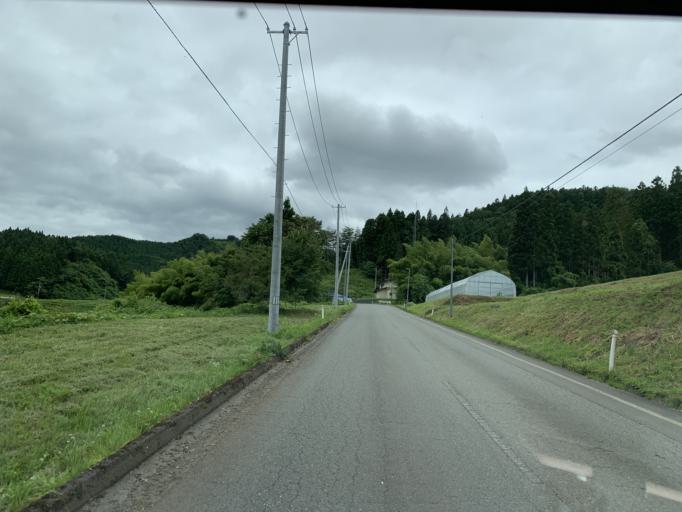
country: JP
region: Iwate
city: Ichinoseki
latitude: 38.9019
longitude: 140.9823
